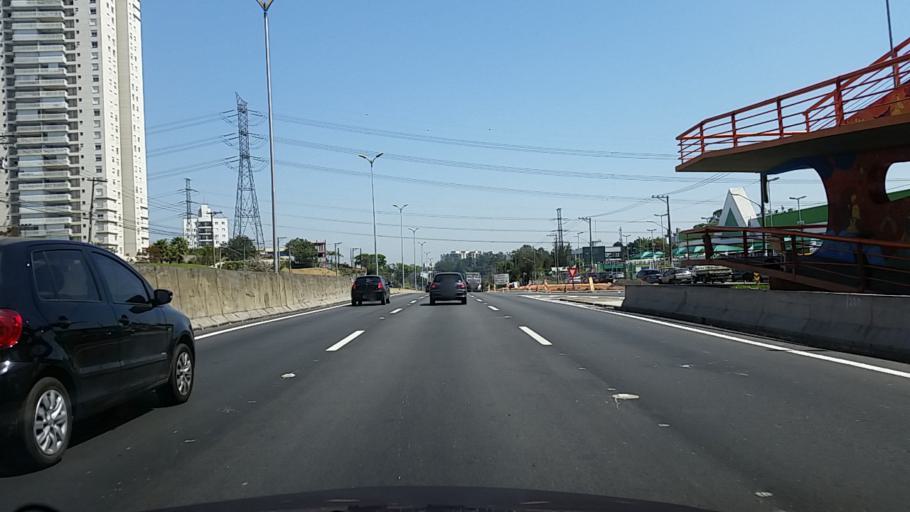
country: BR
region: Sao Paulo
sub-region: Taboao Da Serra
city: Taboao da Serra
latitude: -23.5863
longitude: -46.7509
